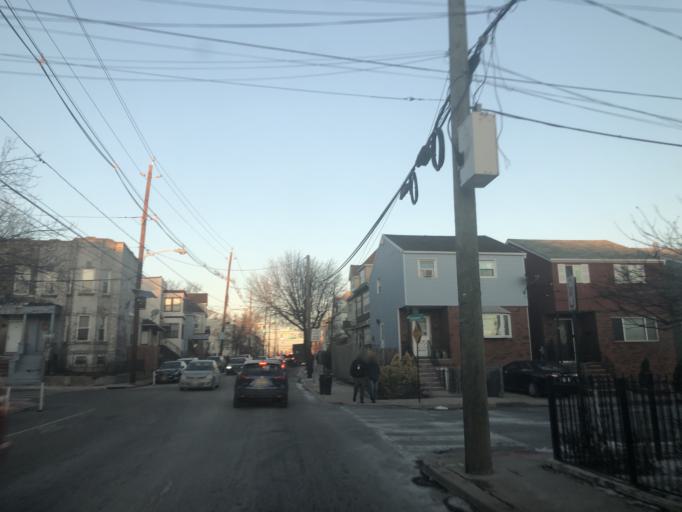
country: US
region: New Jersey
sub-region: Hudson County
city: Jersey City
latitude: 40.7003
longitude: -74.0797
